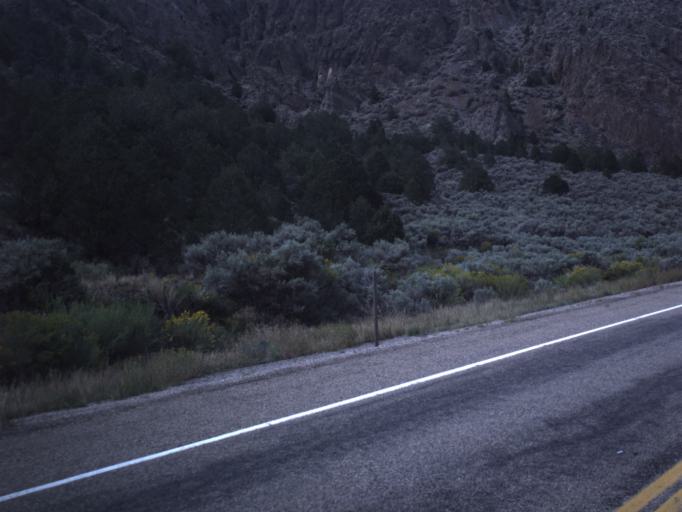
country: US
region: Utah
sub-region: Piute County
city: Junction
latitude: 38.1026
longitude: -112.3363
